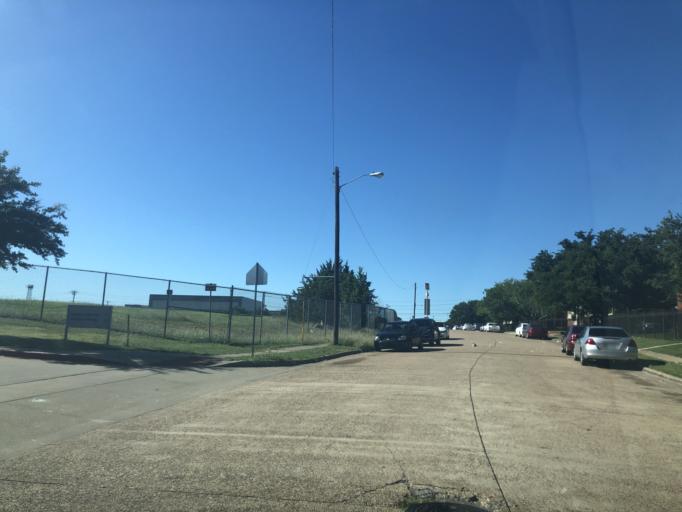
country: US
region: Texas
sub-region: Dallas County
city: Duncanville
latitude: 32.6647
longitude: -96.9296
